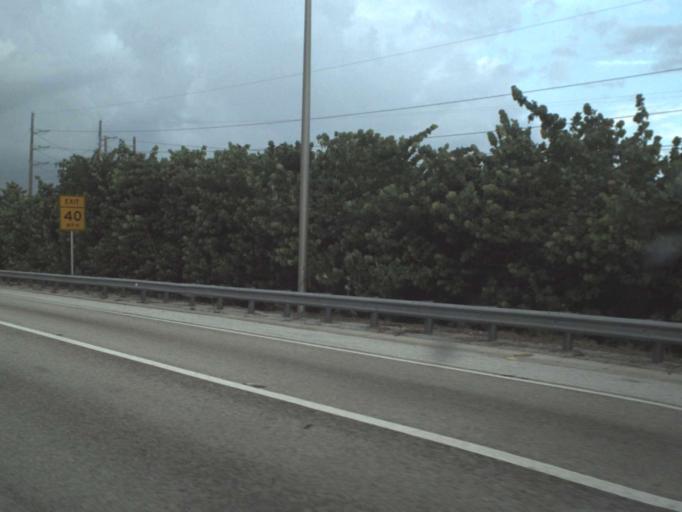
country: US
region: Florida
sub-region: Palm Beach County
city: West Palm Beach
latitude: 26.7025
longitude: -80.0728
